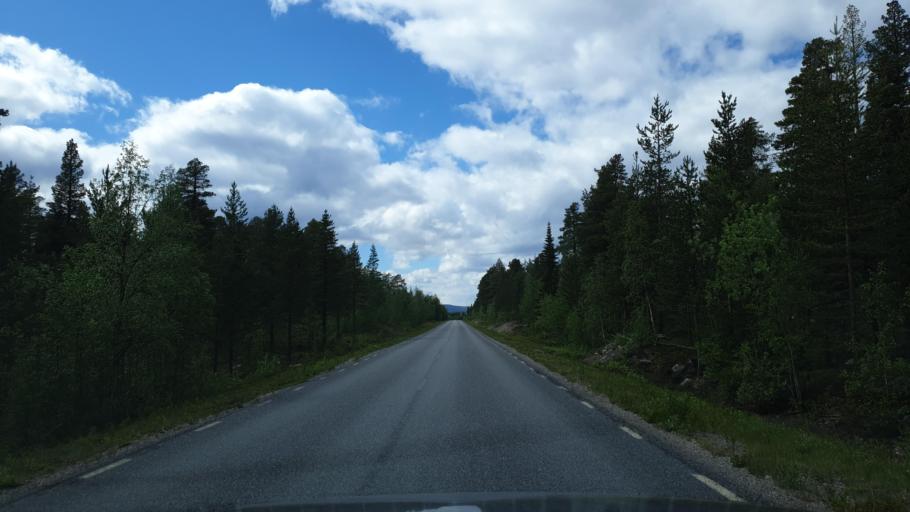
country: SE
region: Norrbotten
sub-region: Jokkmokks Kommun
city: Jokkmokk
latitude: 67.1636
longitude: 19.5097
